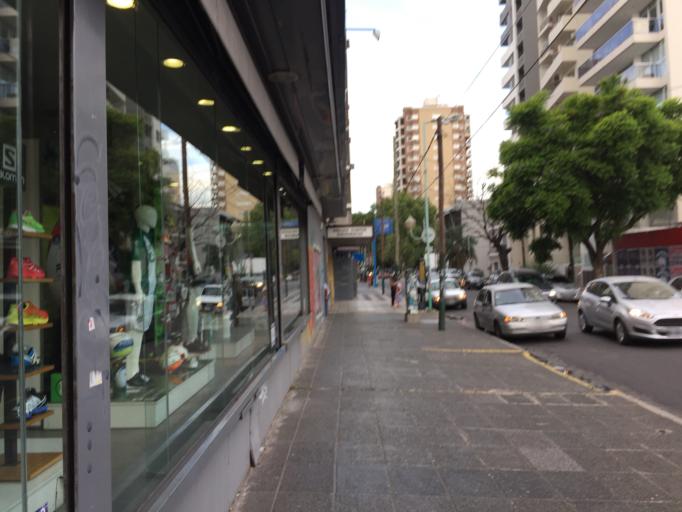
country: AR
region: Buenos Aires
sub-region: Partido de Lomas de Zamora
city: Lomas de Zamora
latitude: -34.7580
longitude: -58.4018
